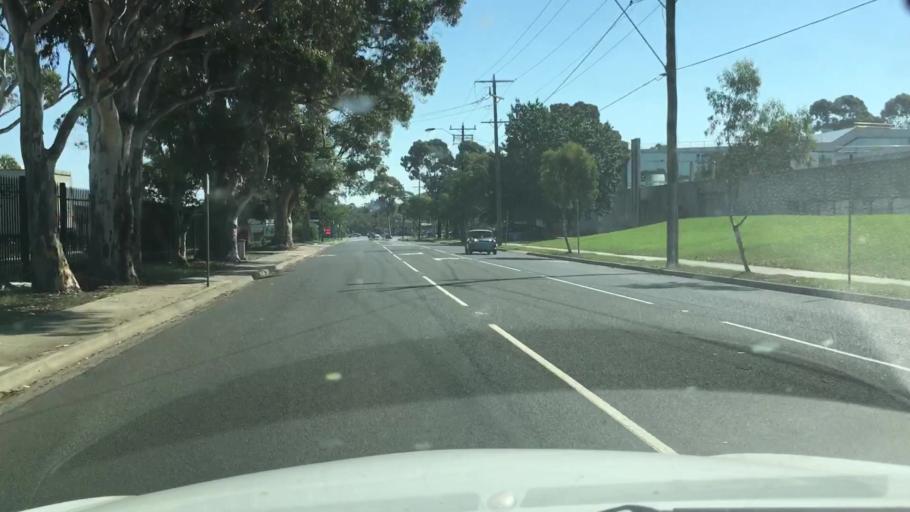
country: AU
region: Victoria
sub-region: Greater Dandenong
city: Noble Park North
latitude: -37.9521
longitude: 145.1818
